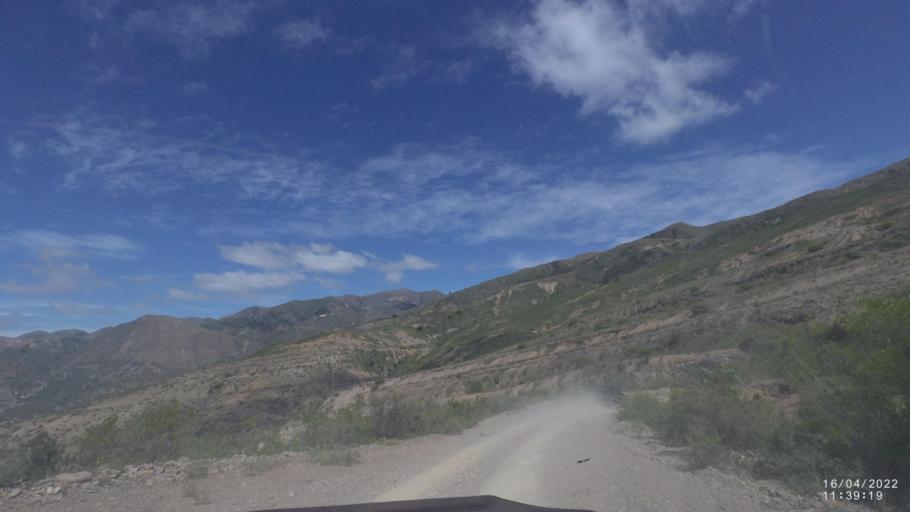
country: BO
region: Cochabamba
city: Mizque
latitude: -17.9661
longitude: -65.6369
